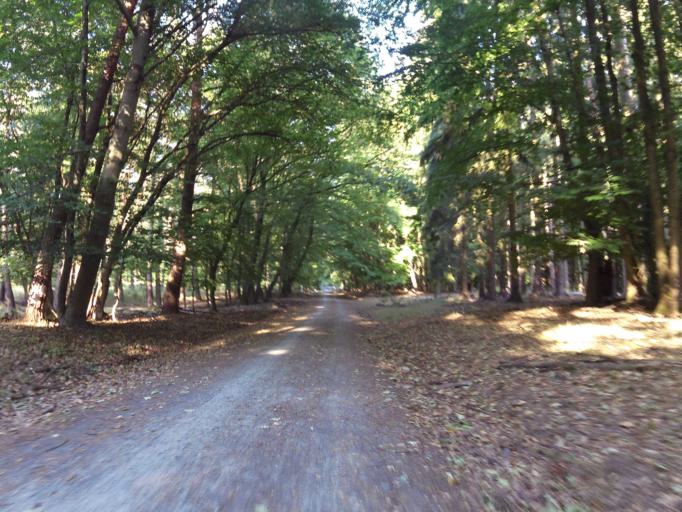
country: DE
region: Hesse
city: Morfelden-Walldorf
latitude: 50.0140
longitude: 8.5600
